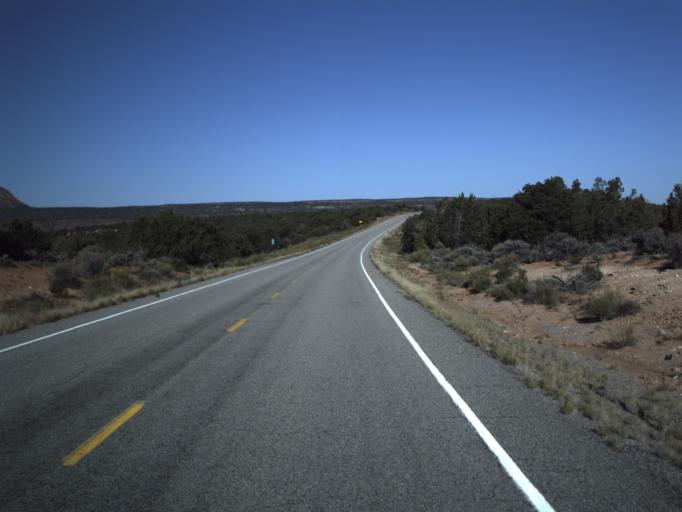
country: US
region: Utah
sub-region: San Juan County
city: Blanding
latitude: 37.5437
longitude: -109.9802
